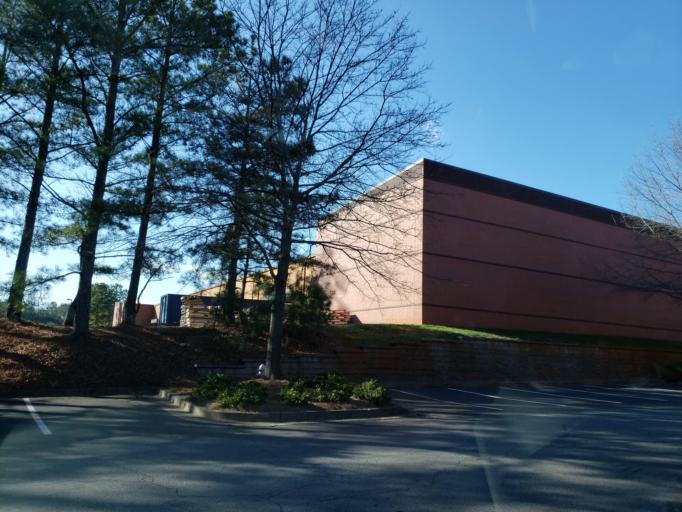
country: US
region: Georgia
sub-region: Cobb County
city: Marietta
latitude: 33.9843
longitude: -84.5205
